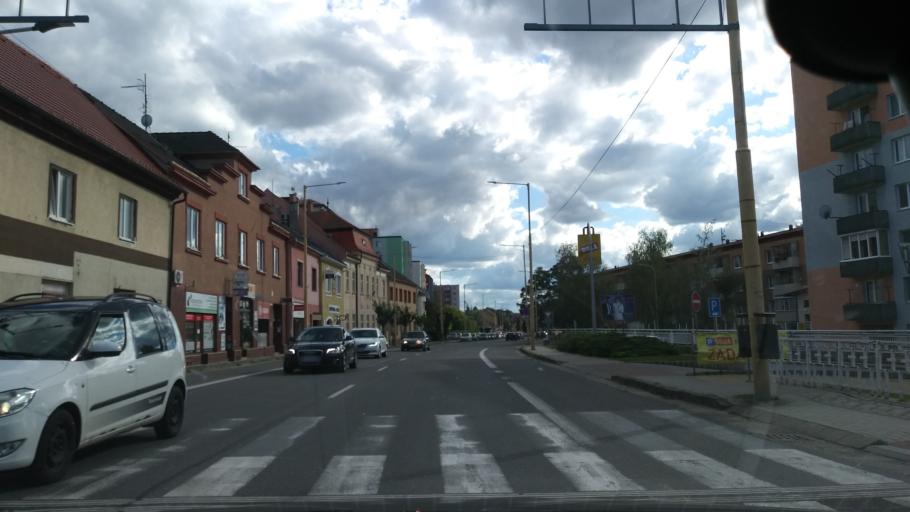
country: SK
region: Trnavsky
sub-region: Okres Skalica
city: Holic
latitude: 48.8081
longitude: 17.1622
